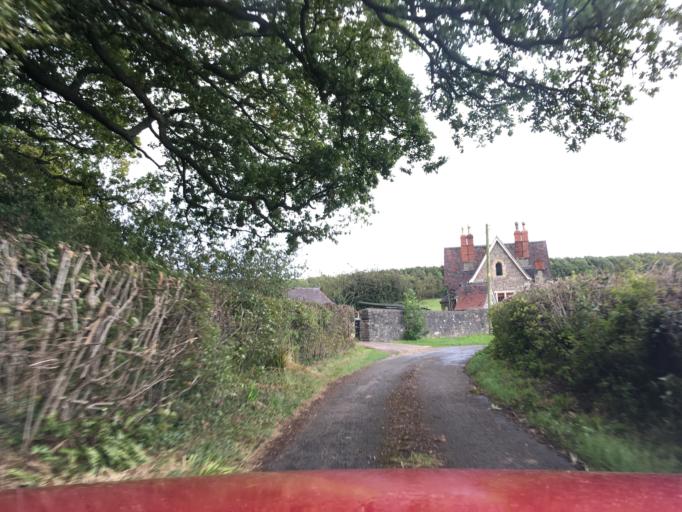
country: GB
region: England
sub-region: South Gloucestershire
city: Falfield
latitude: 51.6266
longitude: -2.4538
